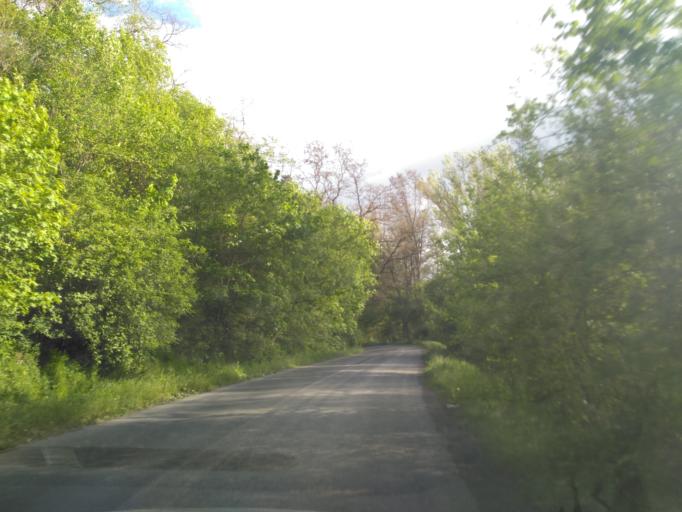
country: CZ
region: Central Bohemia
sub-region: Okres Beroun
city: Kraluv Dvur
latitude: 49.9251
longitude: 14.0475
